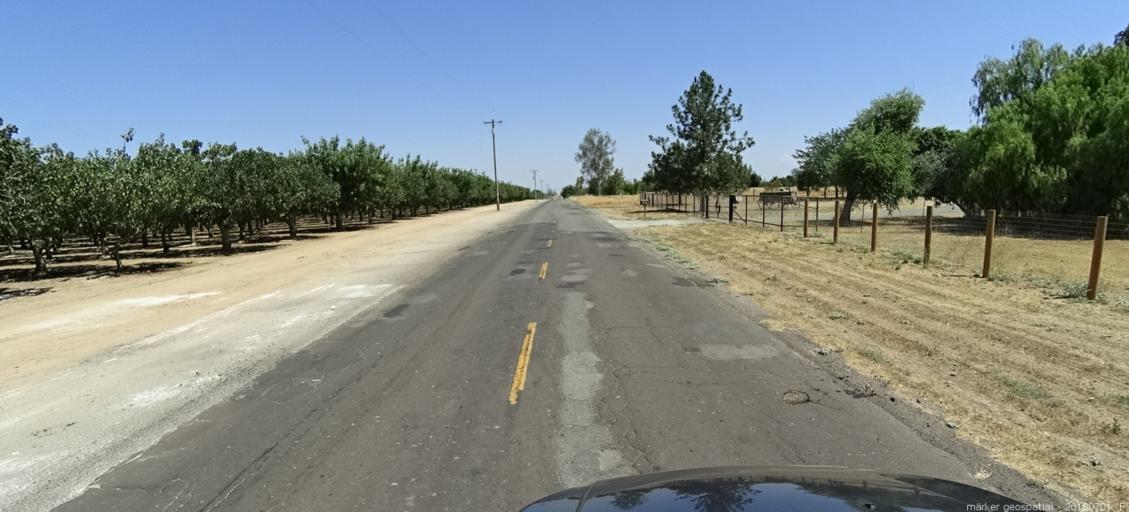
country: US
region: California
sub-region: Madera County
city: Madera Acres
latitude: 37.0627
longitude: -120.0293
